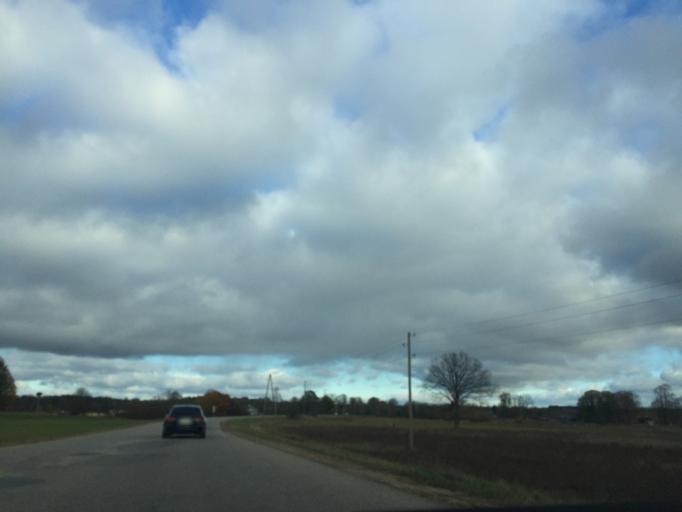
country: LV
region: Carnikava
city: Carnikava
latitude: 57.1140
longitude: 24.3073
